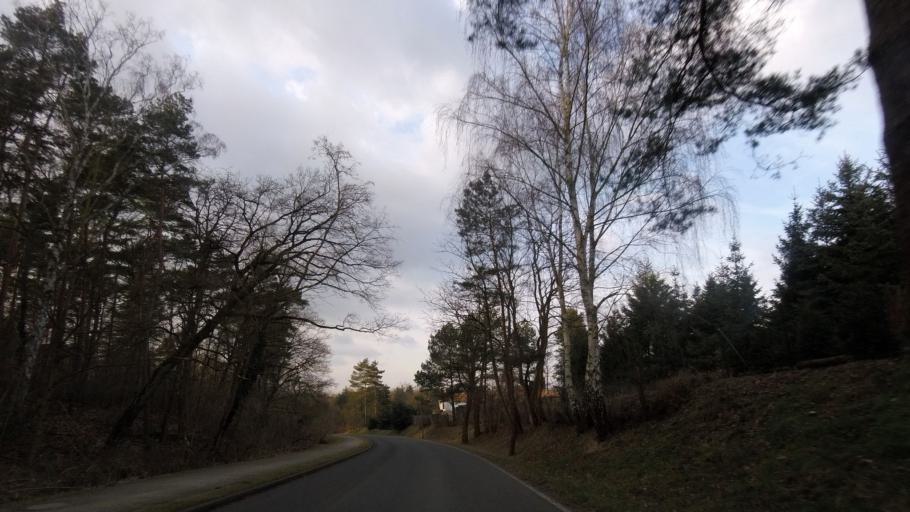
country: DE
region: Brandenburg
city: Belzig
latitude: 52.1343
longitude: 12.5859
